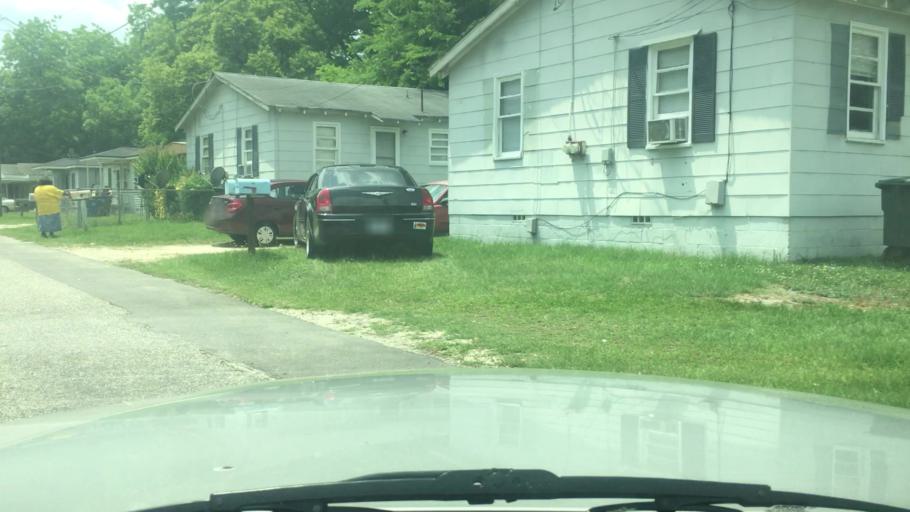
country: US
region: North Carolina
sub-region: Cumberland County
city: Fort Bragg
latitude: 35.0905
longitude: -78.9566
